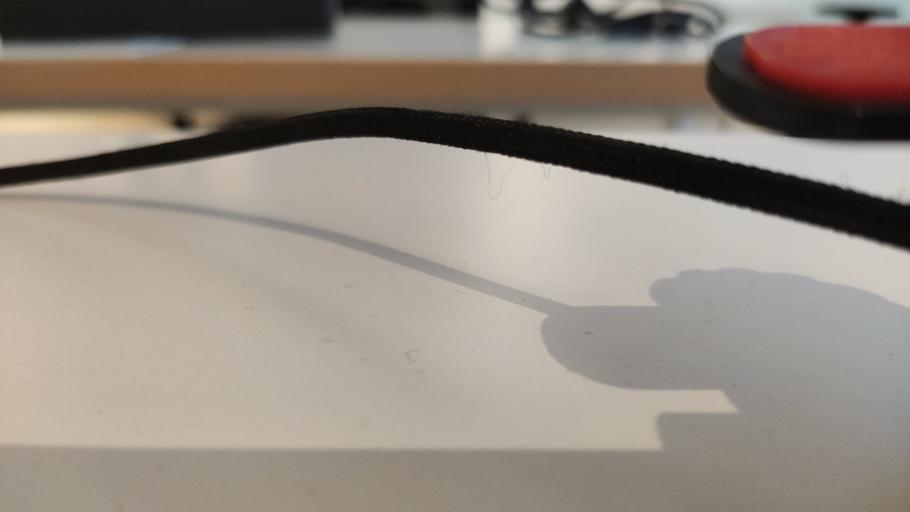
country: RU
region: Moskovskaya
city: Sychevo
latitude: 55.8186
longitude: 36.3029
